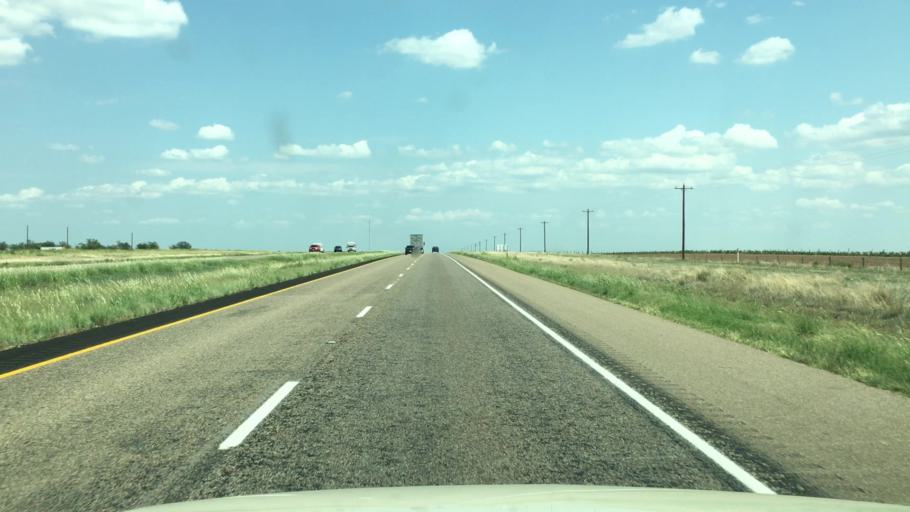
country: US
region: Texas
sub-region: Armstrong County
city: Claude
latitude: 35.0336
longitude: -101.1738
